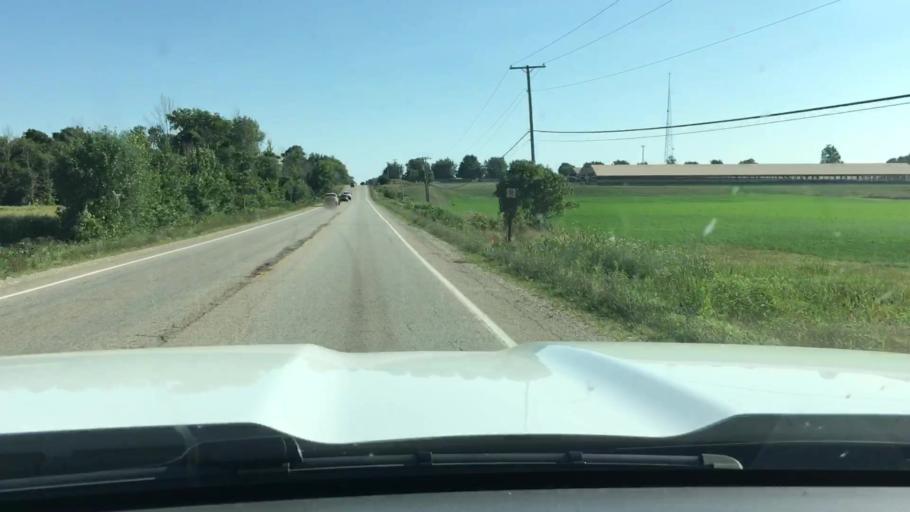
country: US
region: Michigan
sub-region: Ottawa County
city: Allendale
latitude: 43.0112
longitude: -85.9554
